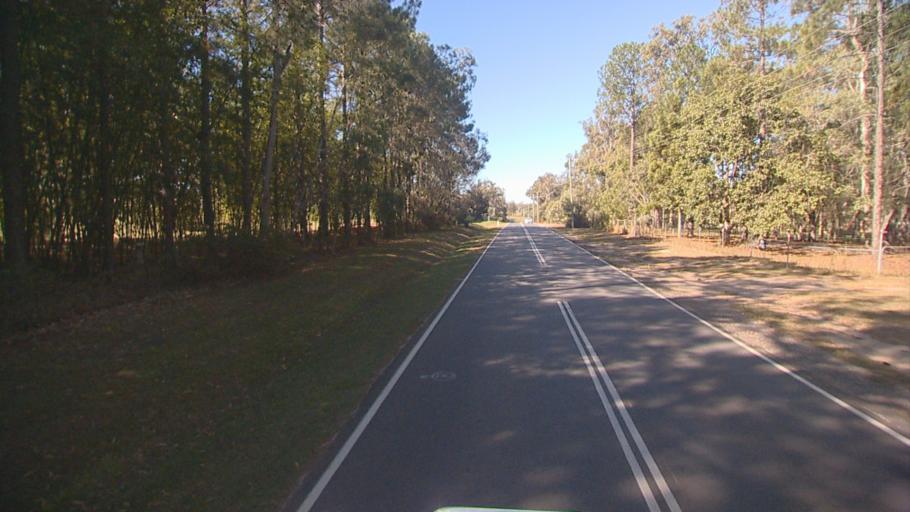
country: AU
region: Queensland
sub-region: Logan
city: Logan Reserve
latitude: -27.7189
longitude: 153.0667
